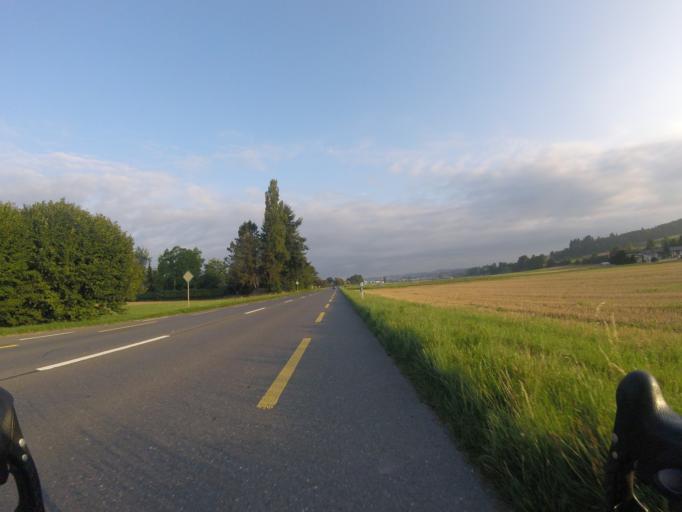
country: CH
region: Bern
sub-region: Bern-Mittelland District
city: Niederwichtrach
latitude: 46.8564
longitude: 7.5703
